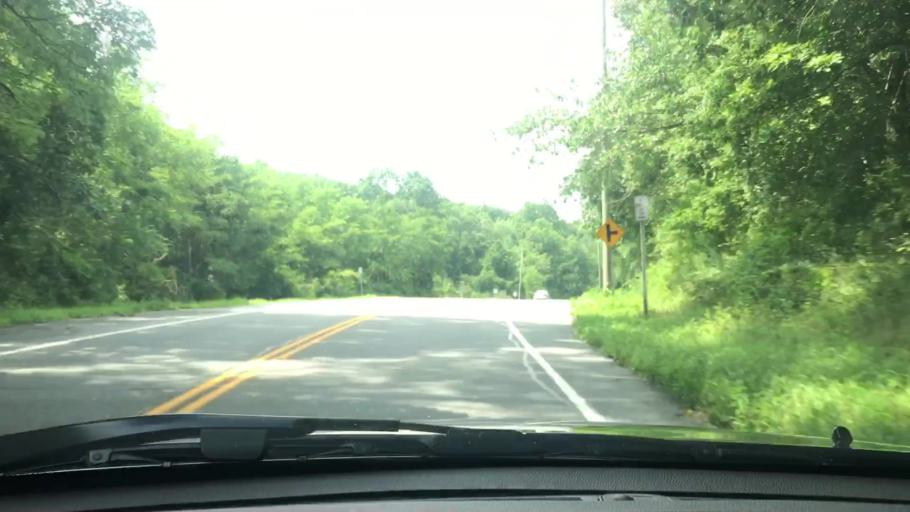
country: US
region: New York
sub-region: Westchester County
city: Bedford
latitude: 41.1931
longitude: -73.6786
